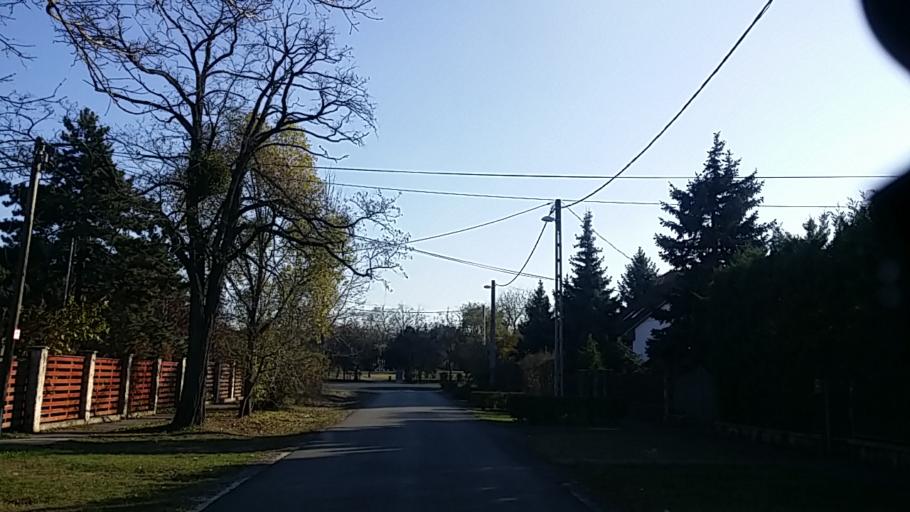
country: HU
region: Budapest
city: Budapest XVIII. keruelet
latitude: 47.4316
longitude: 19.2051
